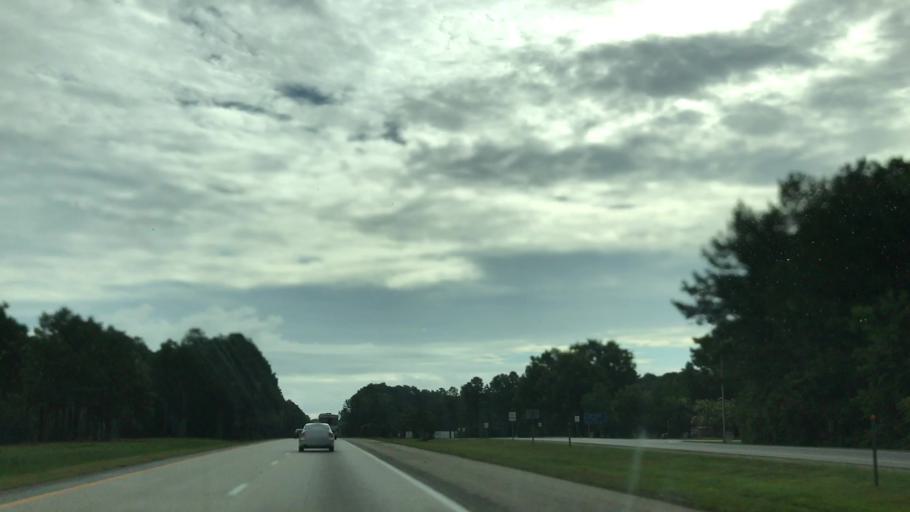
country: US
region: North Carolina
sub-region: Nash County
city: Red Oak
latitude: 36.0247
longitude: -77.8513
